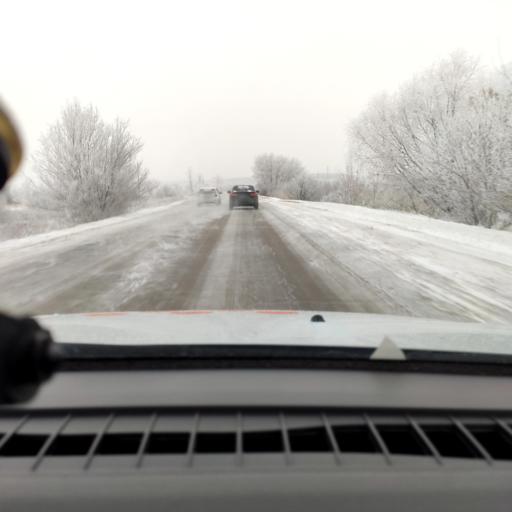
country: RU
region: Samara
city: Samara
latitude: 53.1059
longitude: 50.2268
